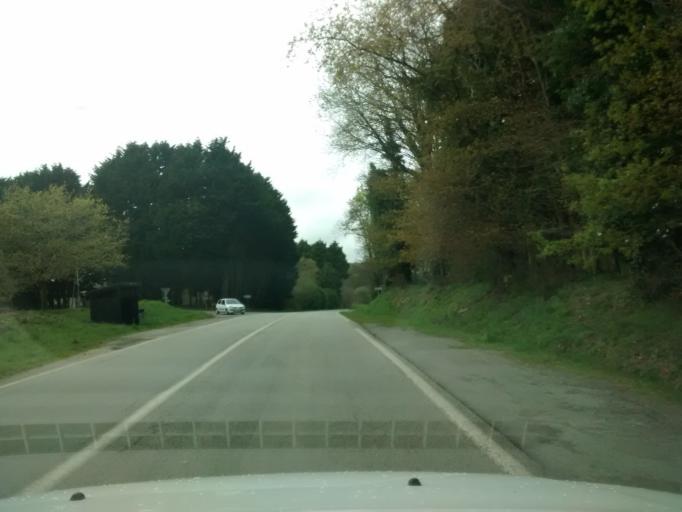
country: FR
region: Brittany
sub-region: Departement du Morbihan
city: Gestel
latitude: 47.7961
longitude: -3.4685
